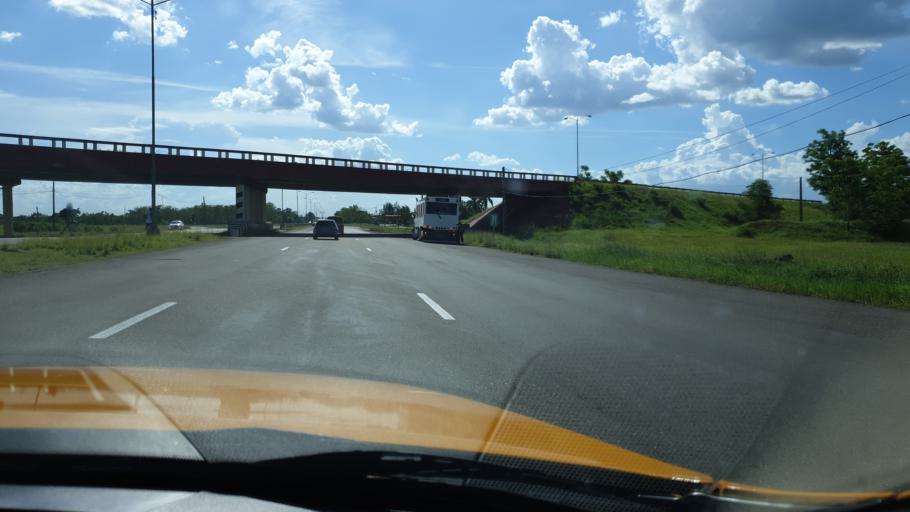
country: CU
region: Cienfuegos
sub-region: Municipio de Aguada de Pasajeros
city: Aguada de Pasajeros
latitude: 22.4036
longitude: -80.8623
